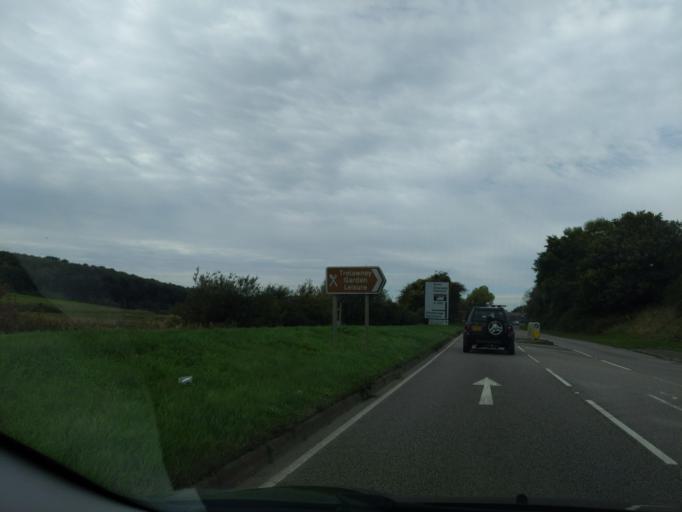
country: GB
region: England
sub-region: Cornwall
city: Wadebridge
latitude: 50.5095
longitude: -4.8117
